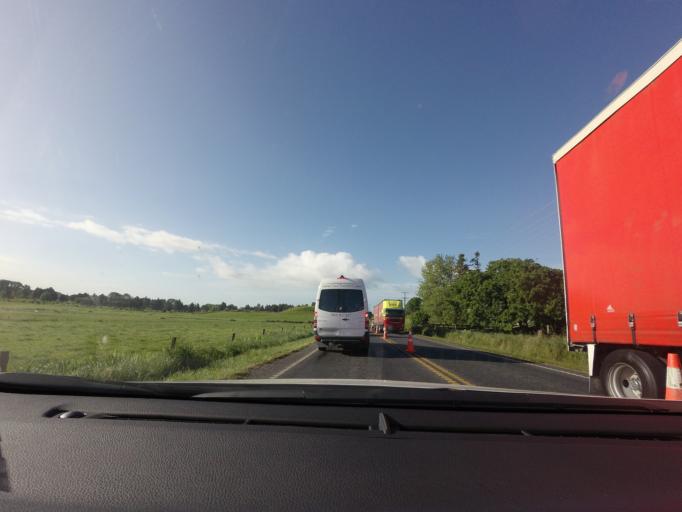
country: NZ
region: Waikato
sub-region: Hauraki District
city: Ngatea
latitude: -37.4695
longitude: 175.5097
